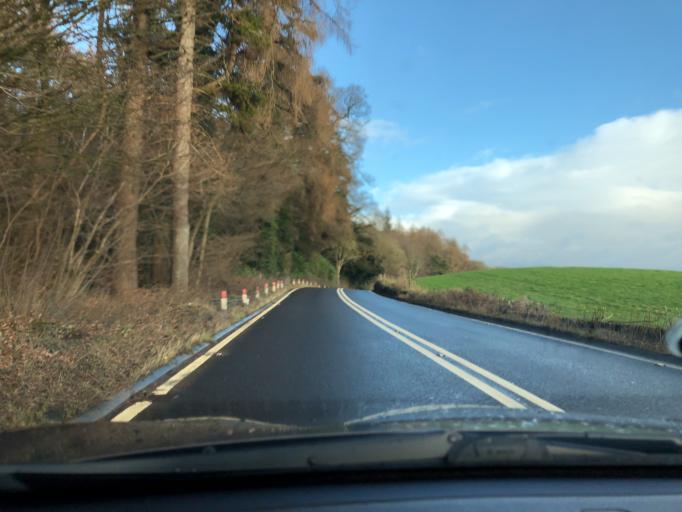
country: GB
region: England
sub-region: Cumbria
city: Ulverston
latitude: 54.2449
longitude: -3.0478
